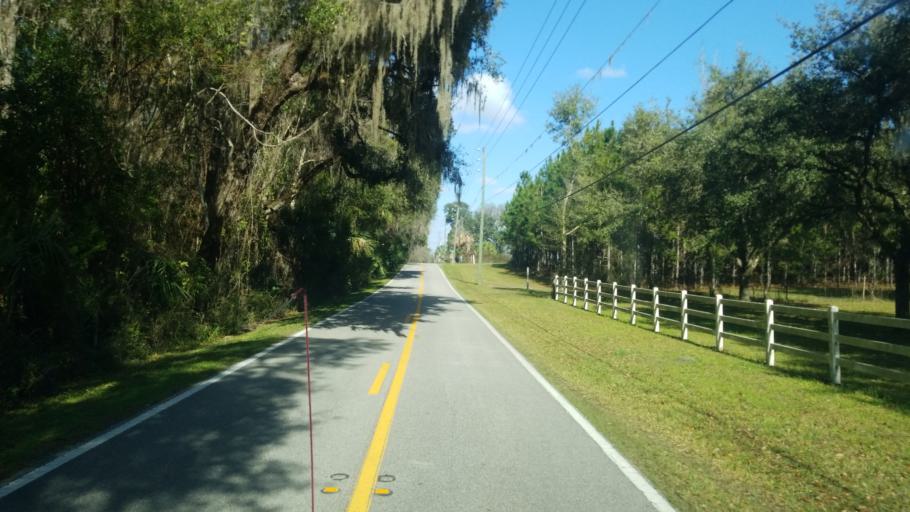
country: US
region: Florida
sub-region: Hernando County
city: North Brooksville
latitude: 28.6160
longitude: -82.3801
